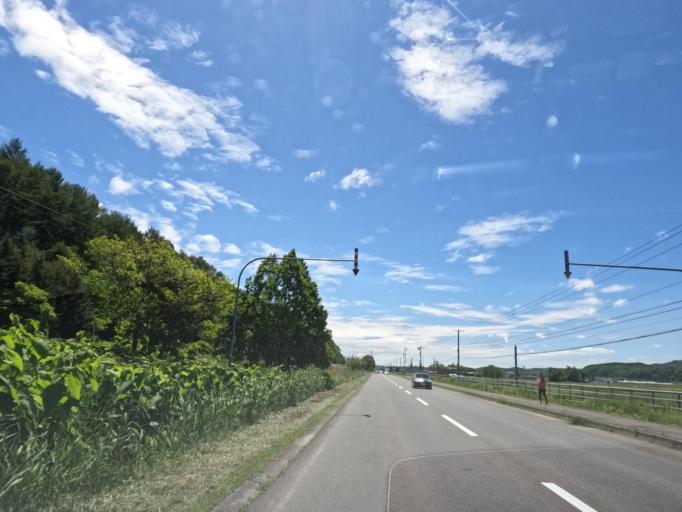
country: JP
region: Hokkaido
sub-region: Asahikawa-shi
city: Asahikawa
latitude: 43.7137
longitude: 142.3753
